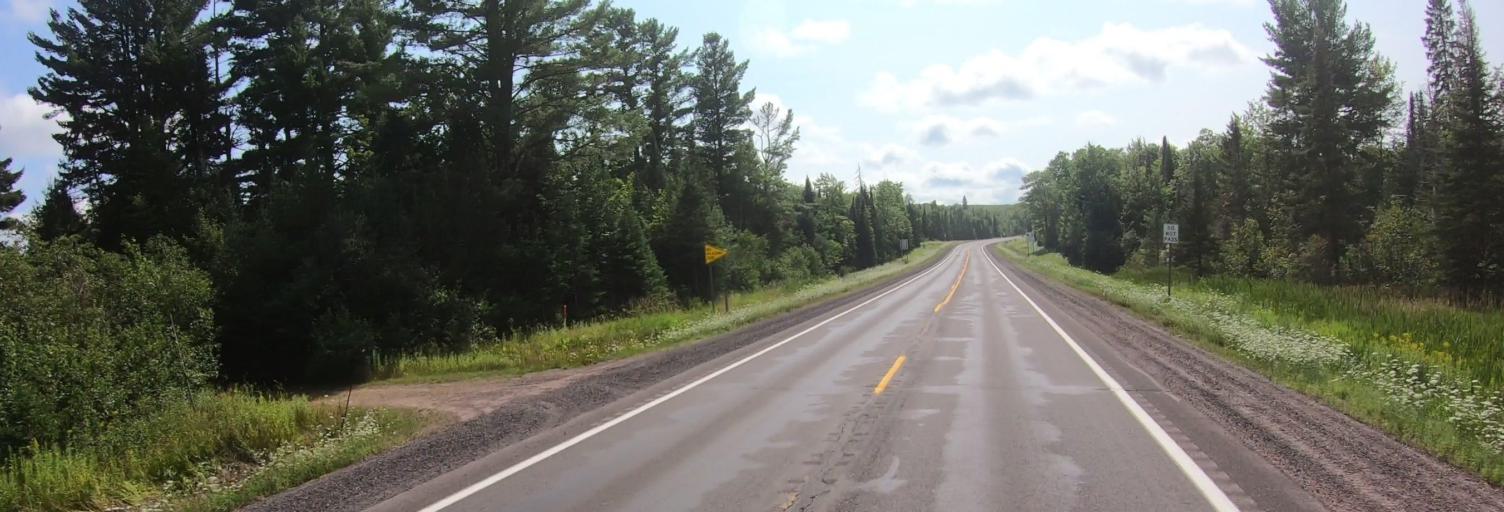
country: US
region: Michigan
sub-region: Ontonagon County
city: Ontonagon
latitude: 46.8536
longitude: -88.9631
